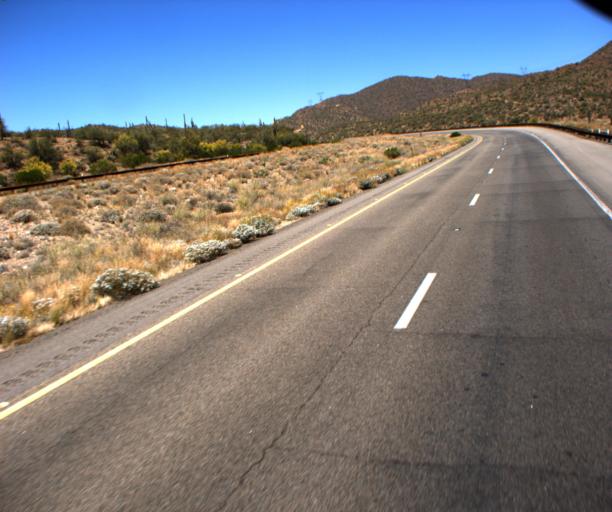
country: US
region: Arizona
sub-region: Yavapai County
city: Bagdad
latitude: 34.3924
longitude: -113.2091
